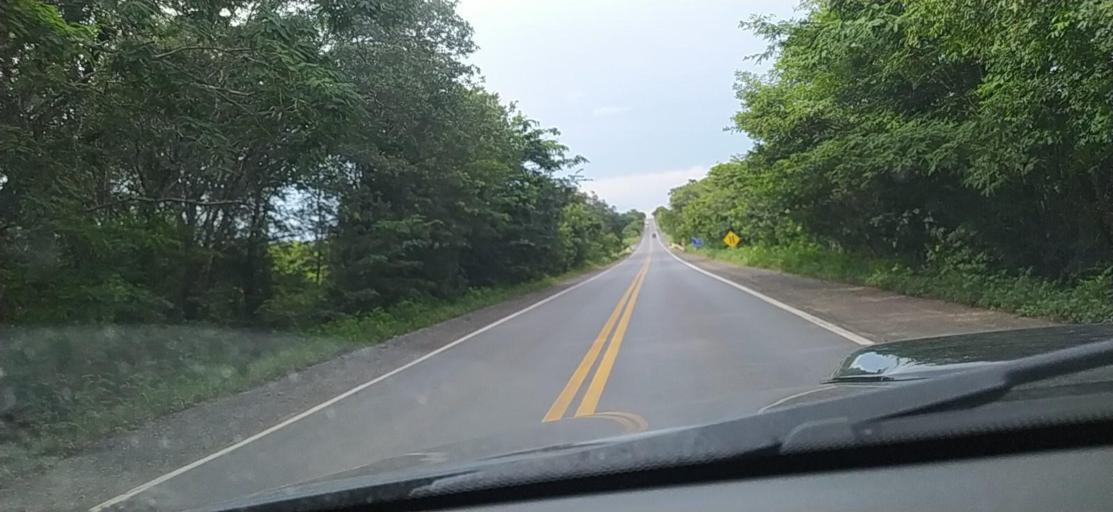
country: BR
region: Minas Gerais
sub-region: Francisco Sa
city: Francisco Sa
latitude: -16.5221
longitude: -43.6803
